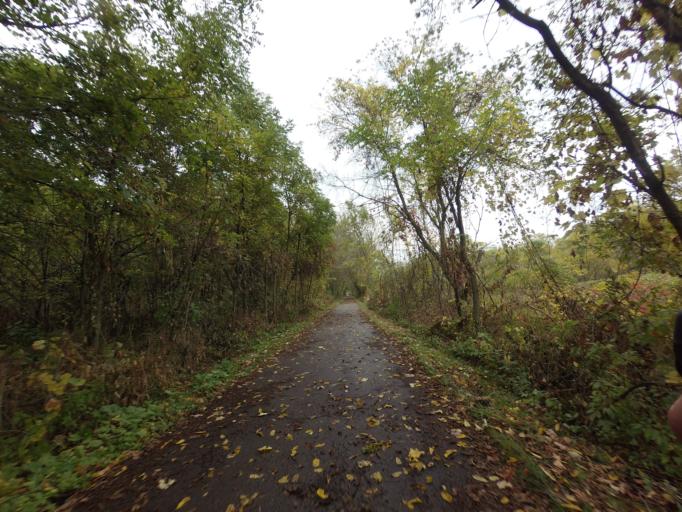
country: CA
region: Ontario
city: Brantford
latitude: 43.1323
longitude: -80.2312
